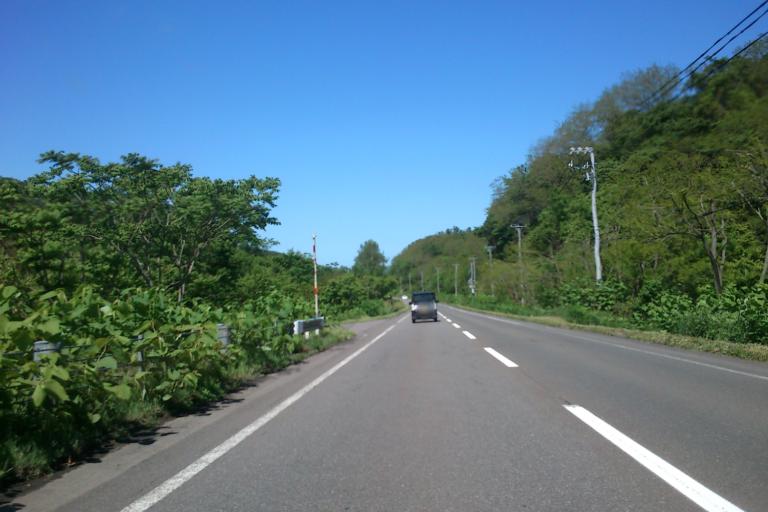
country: JP
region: Hokkaido
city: Ishikari
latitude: 43.5562
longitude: 141.3989
